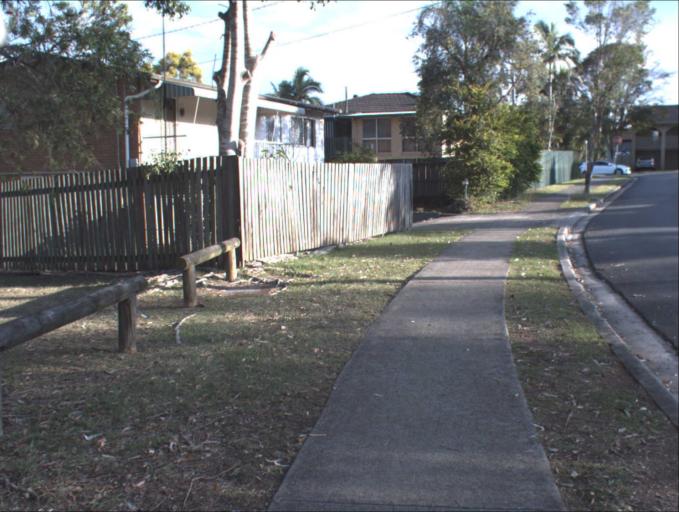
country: AU
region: Queensland
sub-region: Logan
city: Springwood
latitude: -27.6308
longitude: 153.1380
